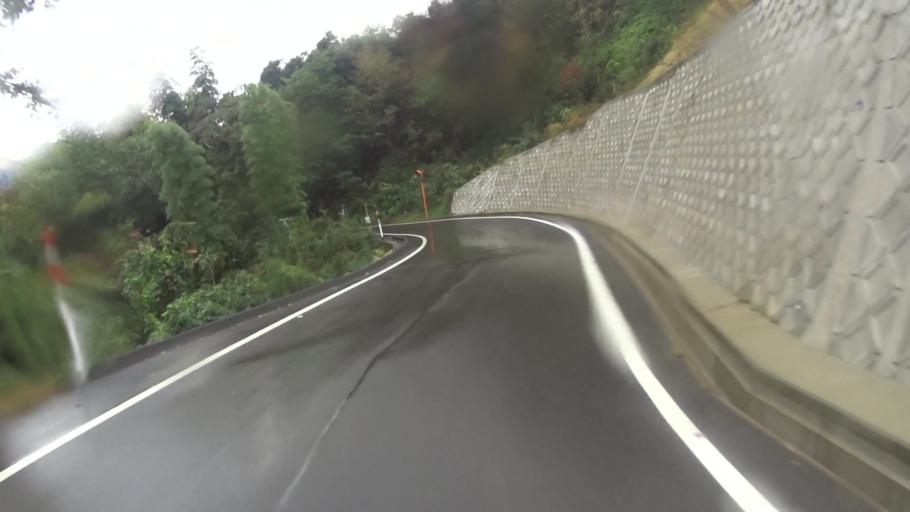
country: JP
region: Kyoto
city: Miyazu
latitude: 35.5297
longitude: 135.2323
